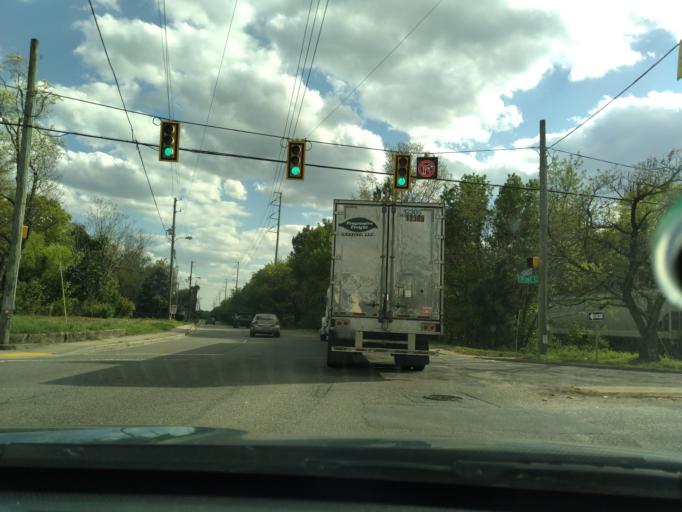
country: US
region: South Carolina
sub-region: Florence County
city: Florence
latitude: 34.1922
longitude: -79.7628
